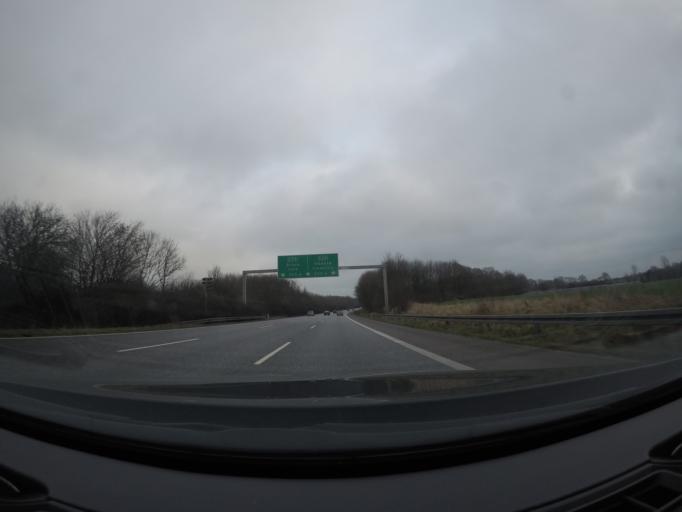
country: DK
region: South Denmark
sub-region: Fredericia Kommune
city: Taulov
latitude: 55.5472
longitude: 9.5427
